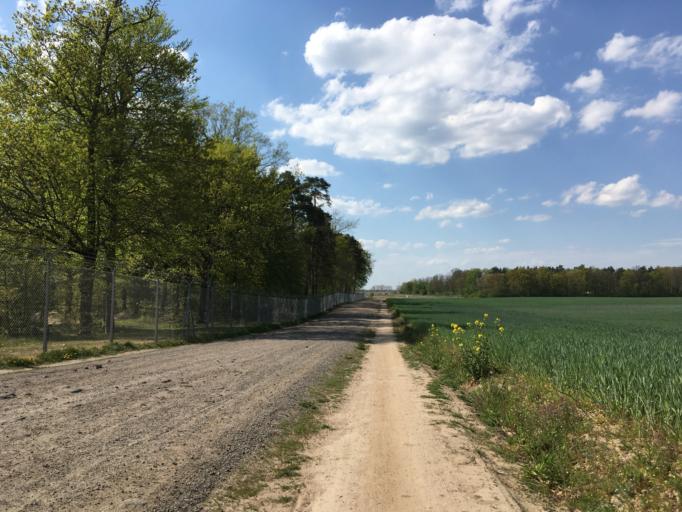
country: DE
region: Brandenburg
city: Ahrensfelde
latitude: 52.5996
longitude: 13.5815
